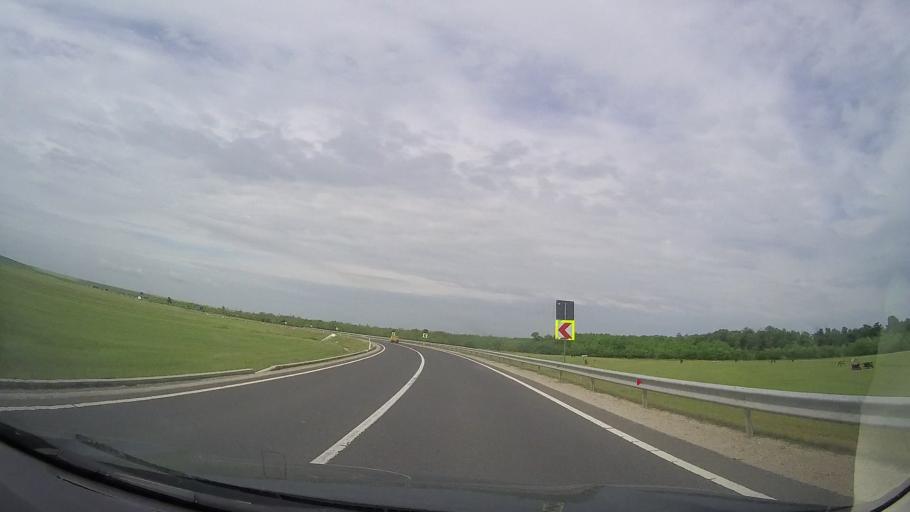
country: RO
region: Teleorman
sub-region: Comuna Buzescu
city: Buzescu
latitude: 44.0209
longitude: 25.2179
